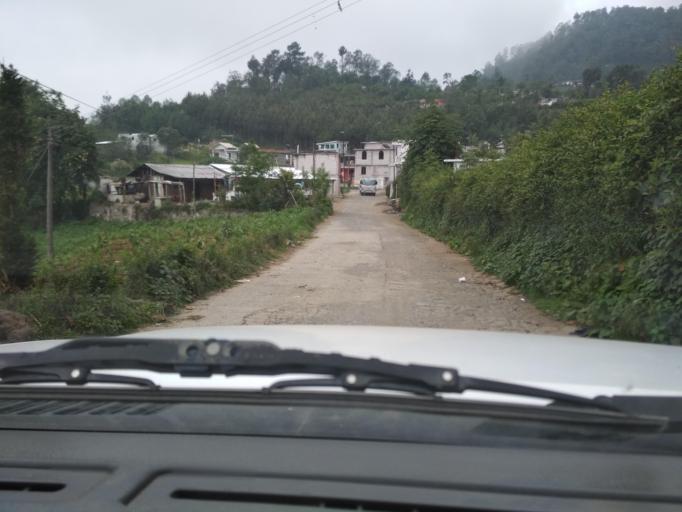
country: MX
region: Veracruz
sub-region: La Perla
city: Chilapa
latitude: 18.9876
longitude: -97.1530
